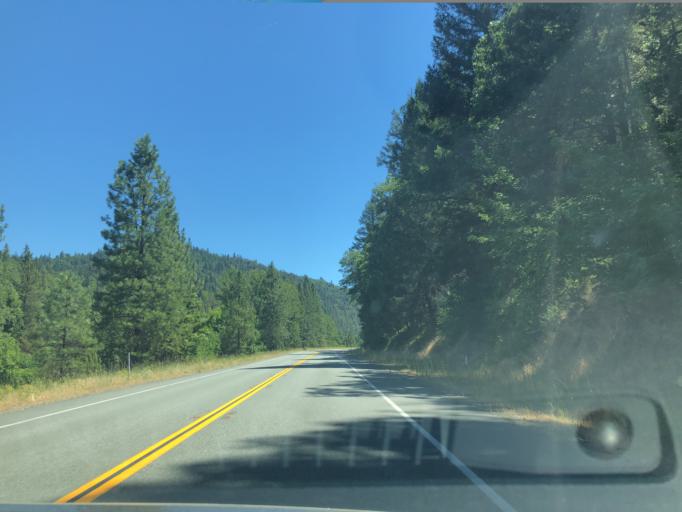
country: US
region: California
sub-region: Trinity County
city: Weaverville
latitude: 40.6529
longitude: -122.9329
